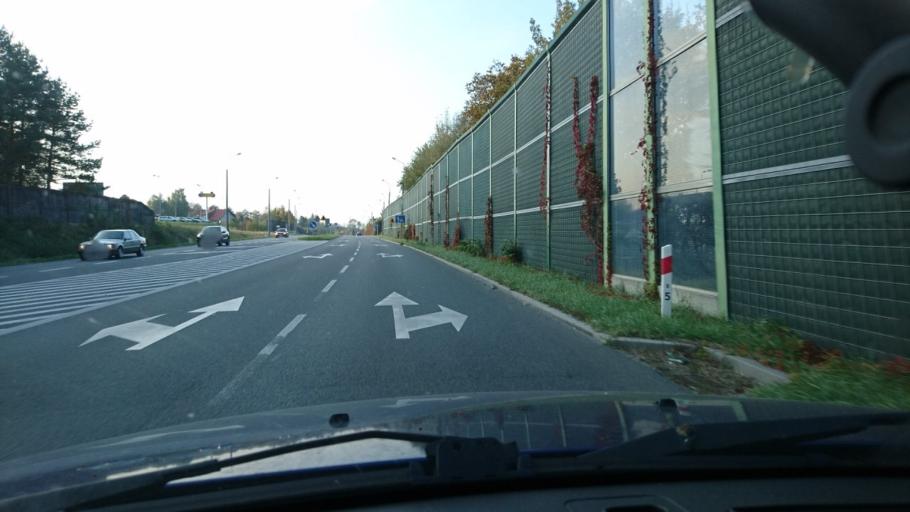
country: PL
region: Silesian Voivodeship
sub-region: Powiat cieszynski
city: Ustron
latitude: 49.7161
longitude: 18.8034
